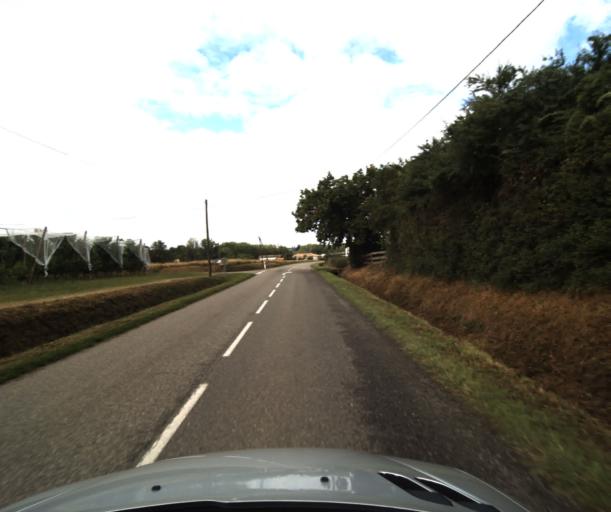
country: FR
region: Midi-Pyrenees
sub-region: Departement du Tarn-et-Garonne
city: Saint-Nicolas-de-la-Grave
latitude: 44.0209
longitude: 1.0150
